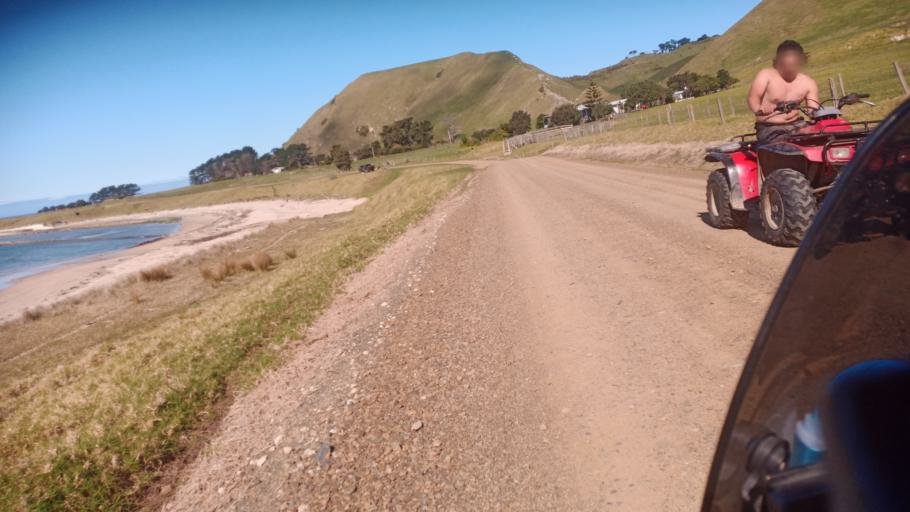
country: NZ
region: Gisborne
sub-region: Gisborne District
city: Gisborne
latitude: -39.0983
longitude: 177.9665
